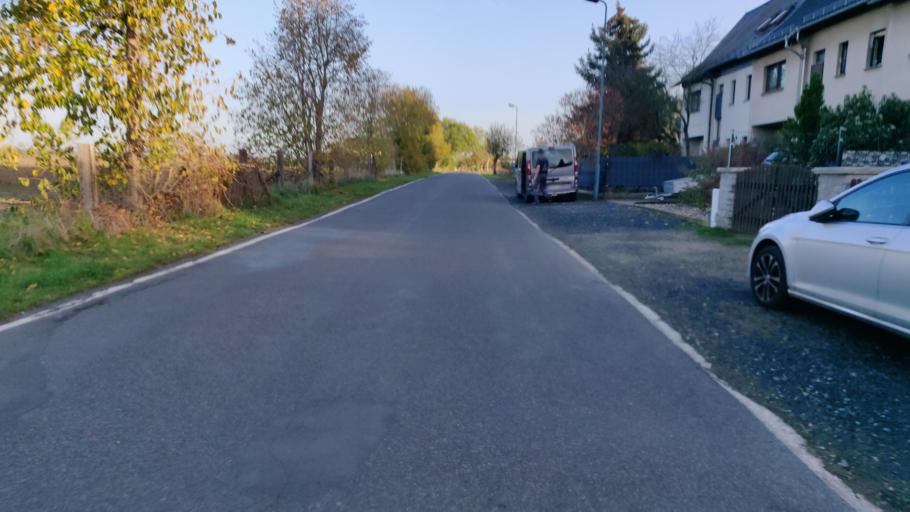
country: DE
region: Saxony
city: Zabeltitz
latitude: 51.3438
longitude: 13.5479
